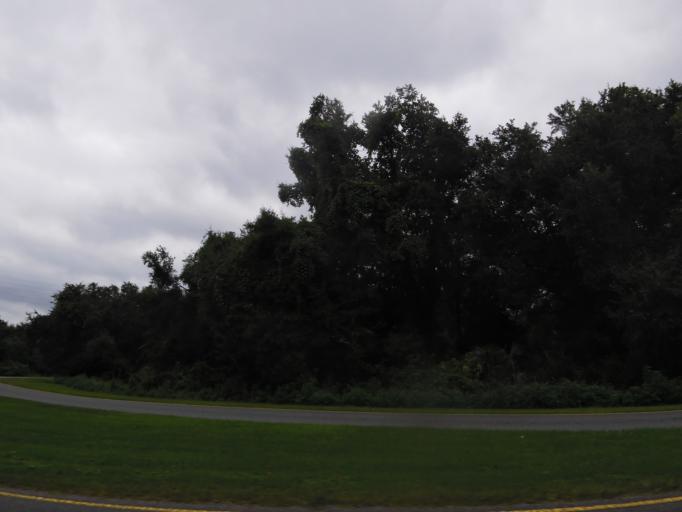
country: US
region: Georgia
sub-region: Glynn County
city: Saint Simon Mills
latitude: 31.1651
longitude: -81.4100
